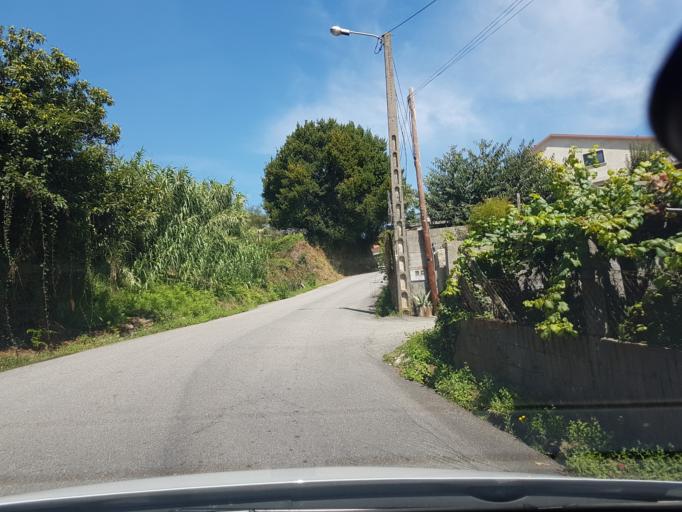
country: ES
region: Galicia
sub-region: Provincia de Pontevedra
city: Porrino
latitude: 42.2177
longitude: -8.6299
